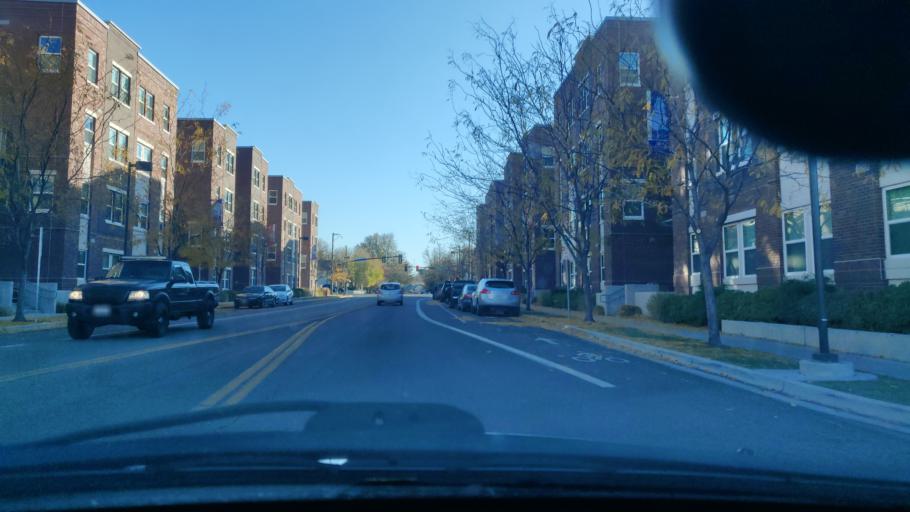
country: US
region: Idaho
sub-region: Ada County
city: Boise
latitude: 43.5997
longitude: -116.2024
